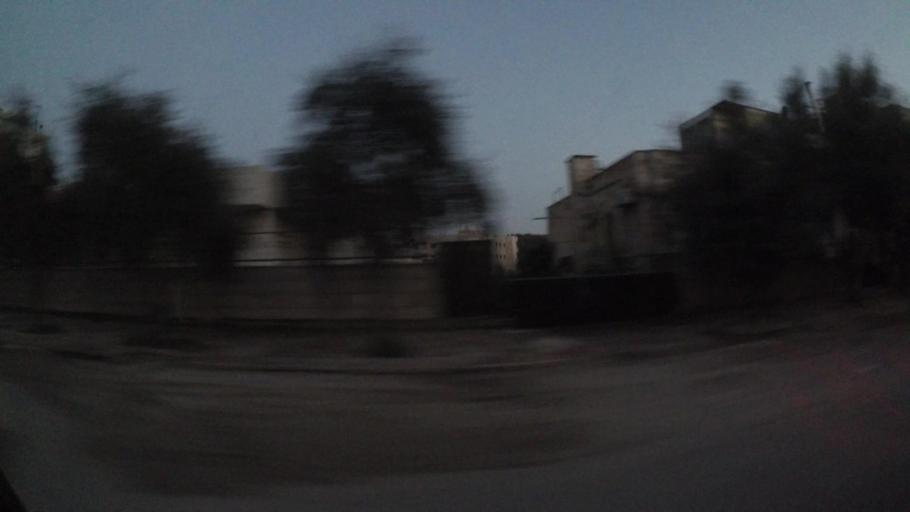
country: JO
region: Amman
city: Al Bunayyat ash Shamaliyah
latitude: 31.8911
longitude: 35.9266
